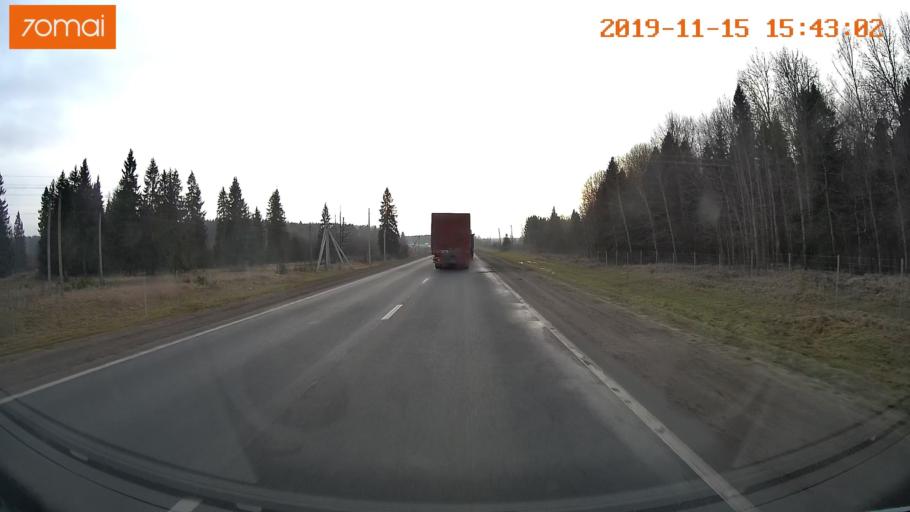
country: RU
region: Jaroslavl
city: Danilov
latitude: 57.9868
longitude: 40.0324
